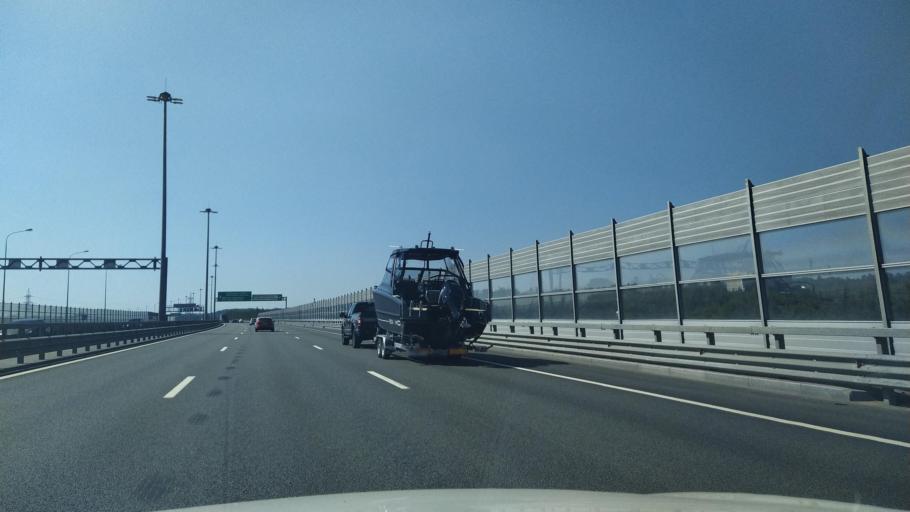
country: RU
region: St.-Petersburg
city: Pargolovo
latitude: 60.0981
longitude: 30.2995
